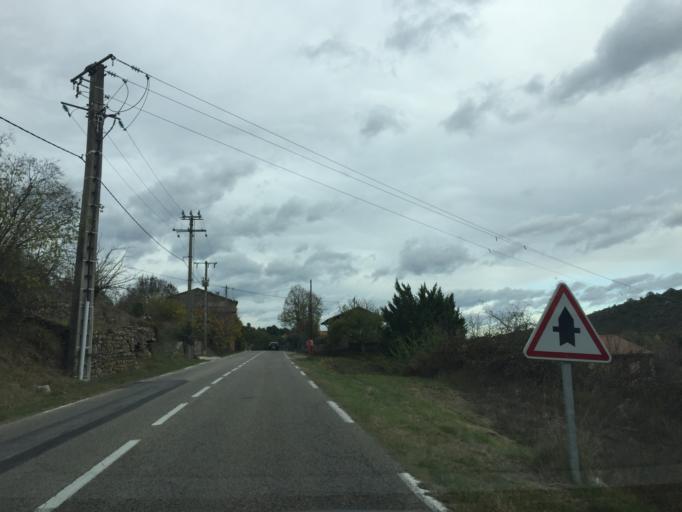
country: FR
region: Rhone-Alpes
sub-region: Departement de l'Ardeche
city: Les Vans
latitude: 44.4205
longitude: 4.1770
